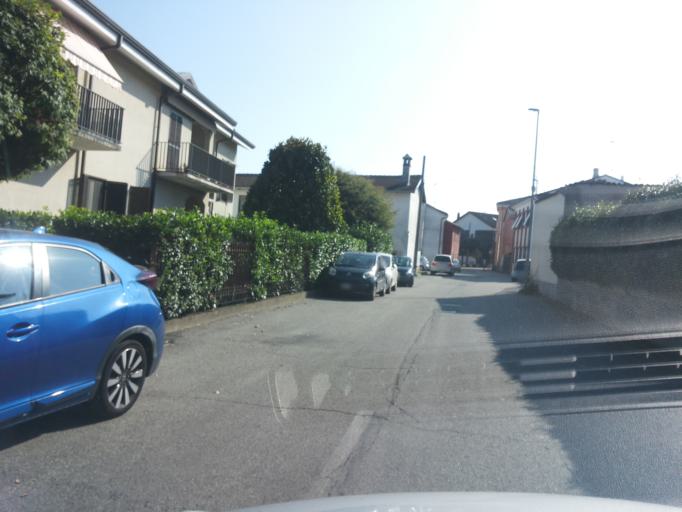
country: IT
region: Piedmont
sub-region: Provincia di Vercelli
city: Prarolo
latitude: 45.3033
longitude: 8.4542
